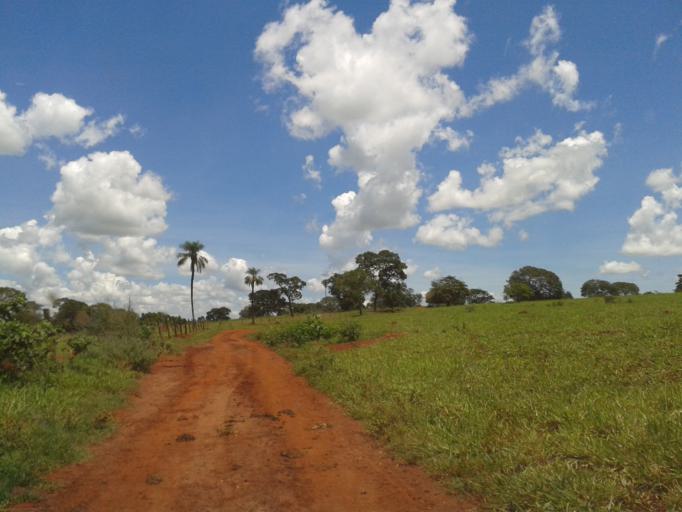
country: BR
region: Minas Gerais
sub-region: Santa Vitoria
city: Santa Vitoria
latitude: -18.7938
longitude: -49.8428
